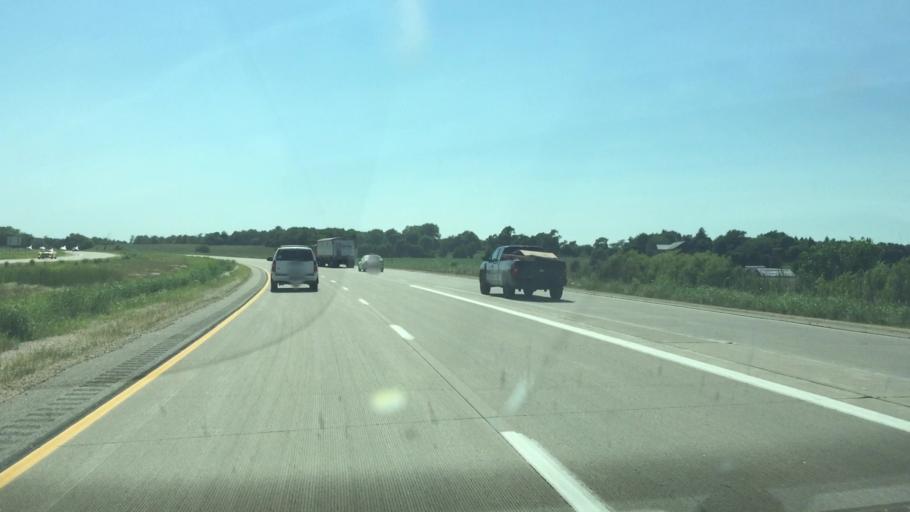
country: US
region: Iowa
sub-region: Jones County
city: Monticello
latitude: 42.2069
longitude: -91.1959
